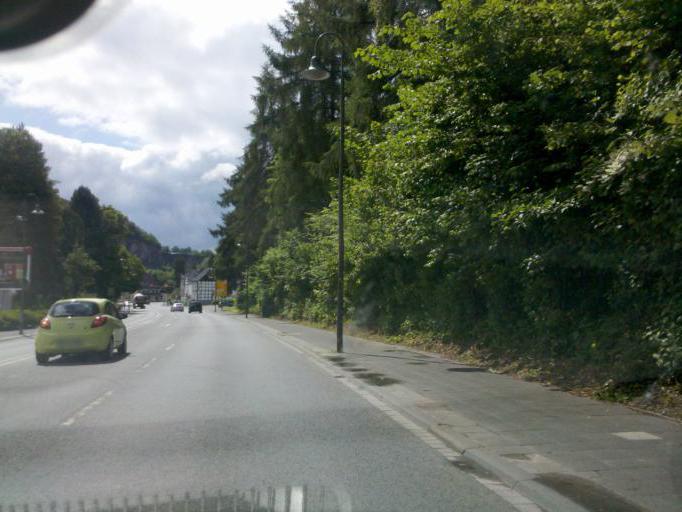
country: DE
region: North Rhine-Westphalia
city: Warstein
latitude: 51.4523
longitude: 8.3533
